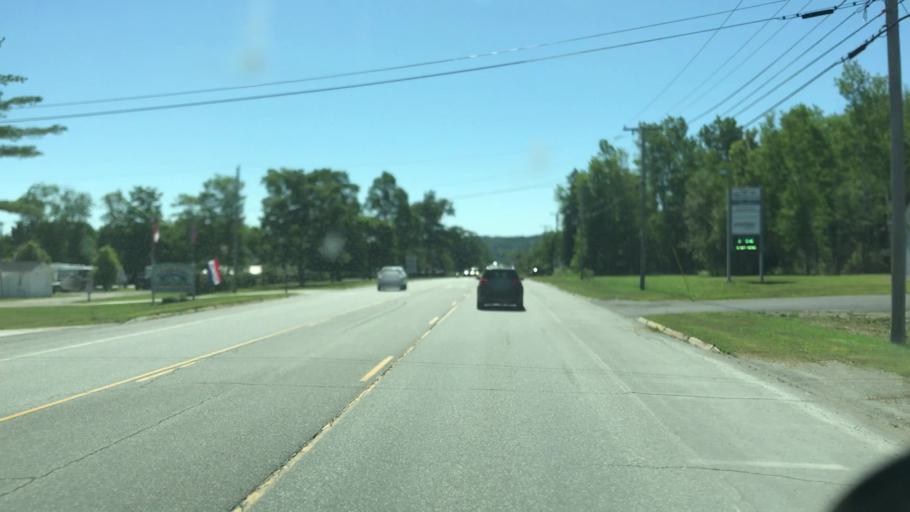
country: US
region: Maine
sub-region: Penobscot County
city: Holden
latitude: 44.7640
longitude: -68.7044
